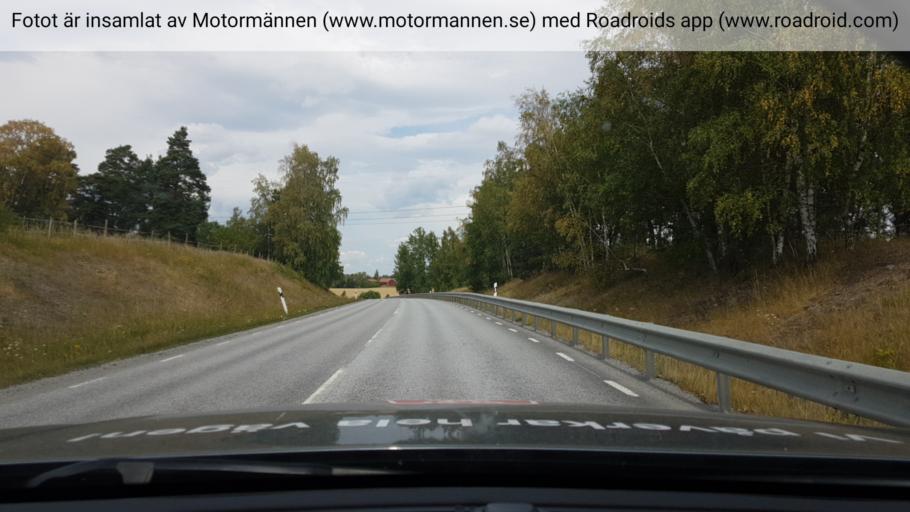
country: SE
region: Uppsala
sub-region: Habo Kommun
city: Balsta
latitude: 59.6168
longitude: 17.6065
